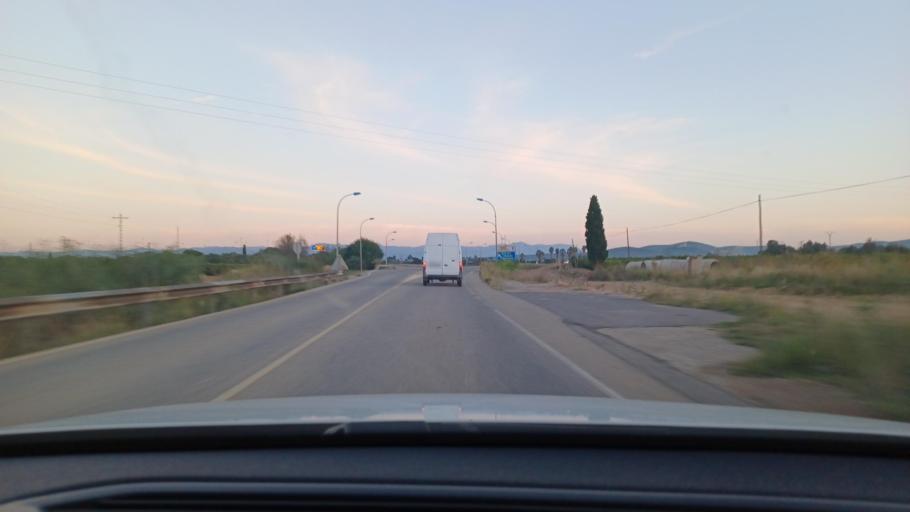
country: ES
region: Catalonia
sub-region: Provincia de Tarragona
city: Ulldecona
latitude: 40.5517
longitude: 0.4328
